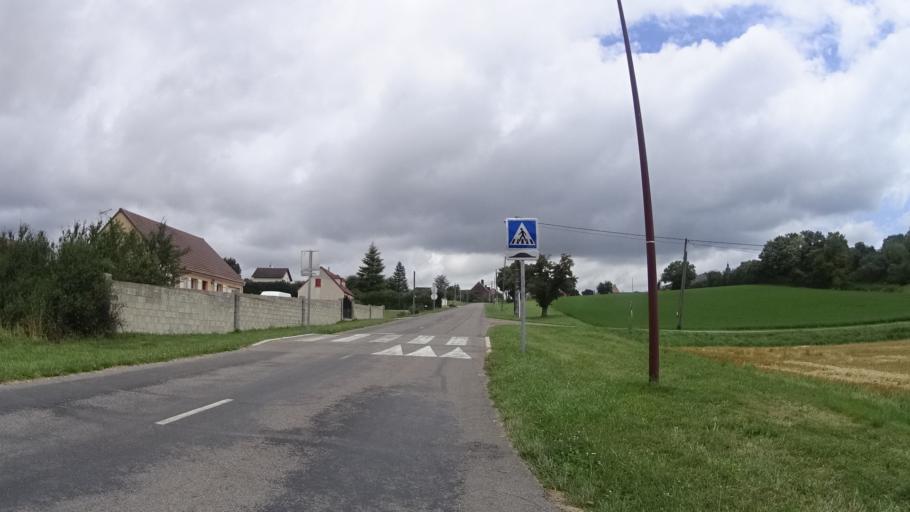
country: FR
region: Champagne-Ardenne
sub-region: Departement de l'Aube
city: Bouilly
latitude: 48.1194
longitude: 3.9912
